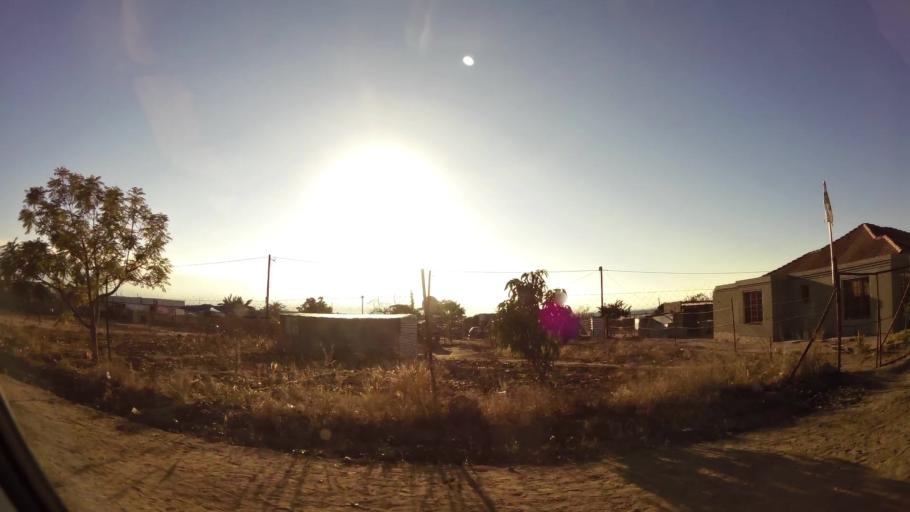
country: ZA
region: Limpopo
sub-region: Capricorn District Municipality
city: Polokwane
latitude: -23.8381
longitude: 29.3636
